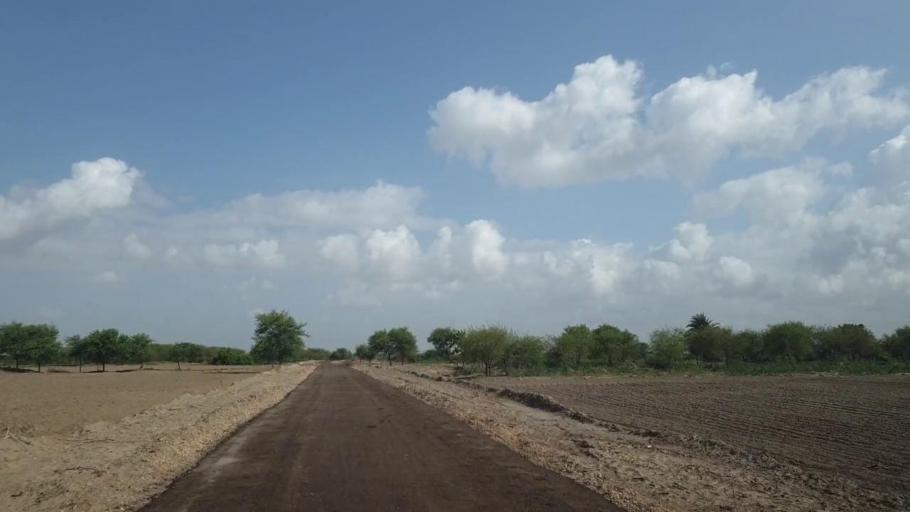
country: PK
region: Sindh
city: Kadhan
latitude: 24.5401
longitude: 69.0656
